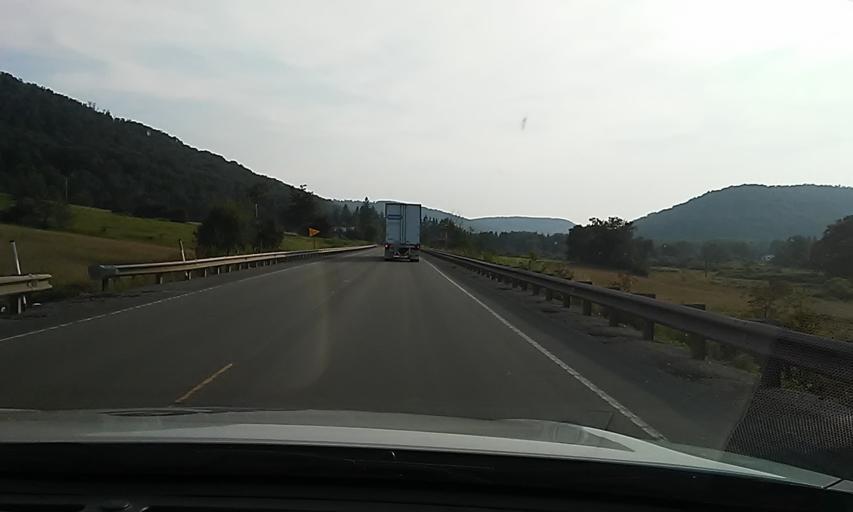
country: US
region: Pennsylvania
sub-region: McKean County
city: Smethport
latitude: 41.7210
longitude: -78.5527
